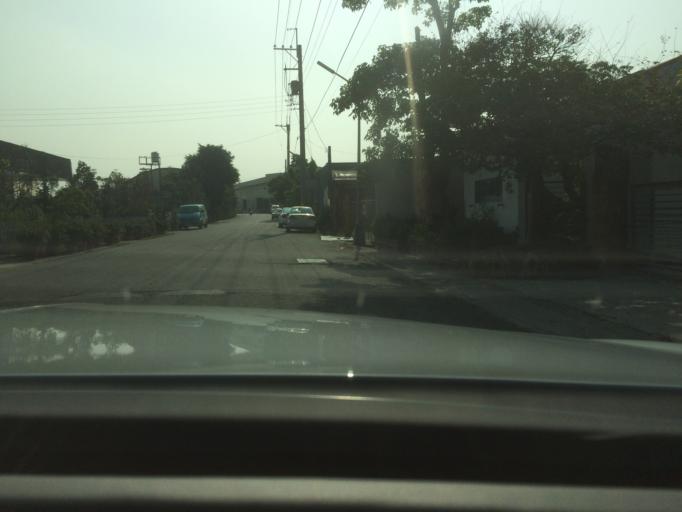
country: TW
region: Taiwan
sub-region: Nantou
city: Nantou
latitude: 23.9088
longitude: 120.5251
